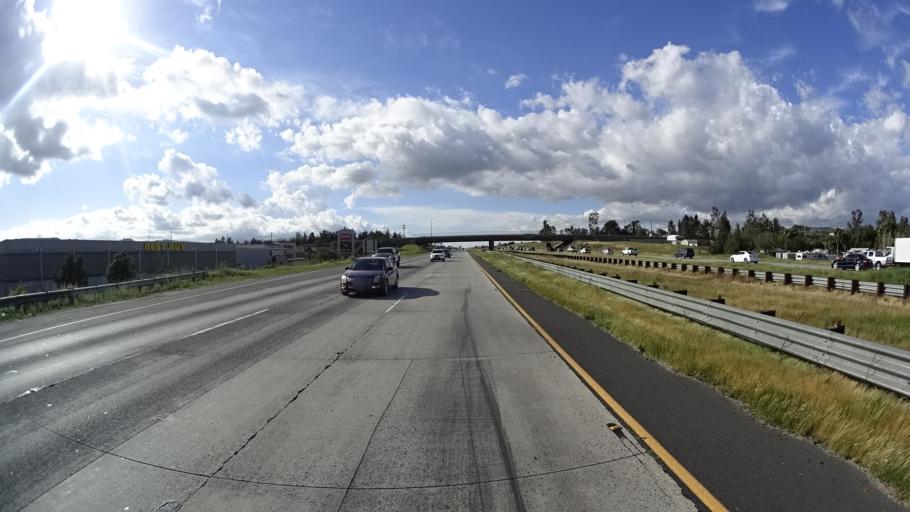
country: US
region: California
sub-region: Riverside County
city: Murrieta
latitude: 33.5584
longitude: -117.1980
